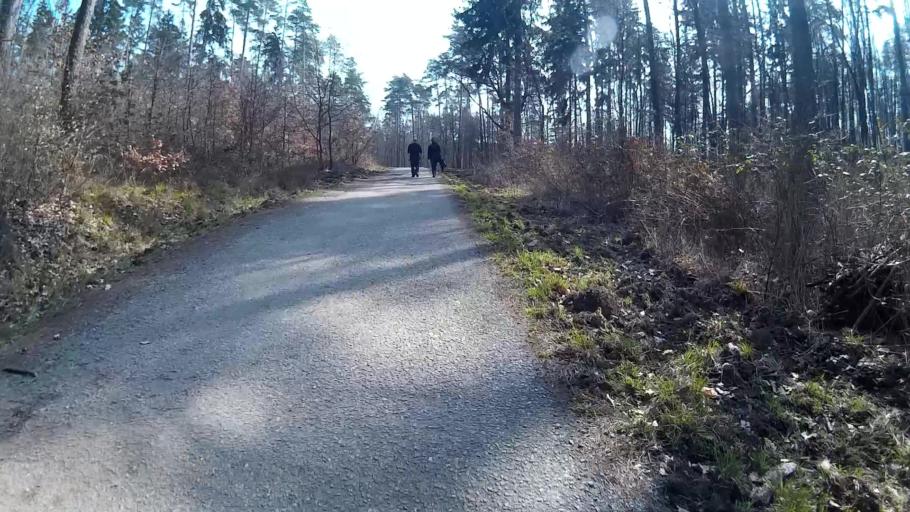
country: CZ
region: South Moravian
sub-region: Mesto Brno
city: Mokra Hora
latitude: 49.2560
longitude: 16.6064
